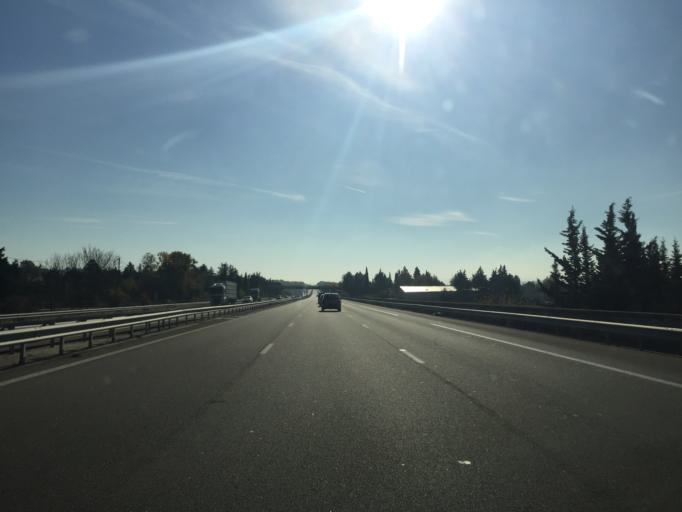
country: FR
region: Provence-Alpes-Cote d'Azur
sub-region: Departement du Vaucluse
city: Morieres-les-Avignon
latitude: 43.9416
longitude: 4.9114
